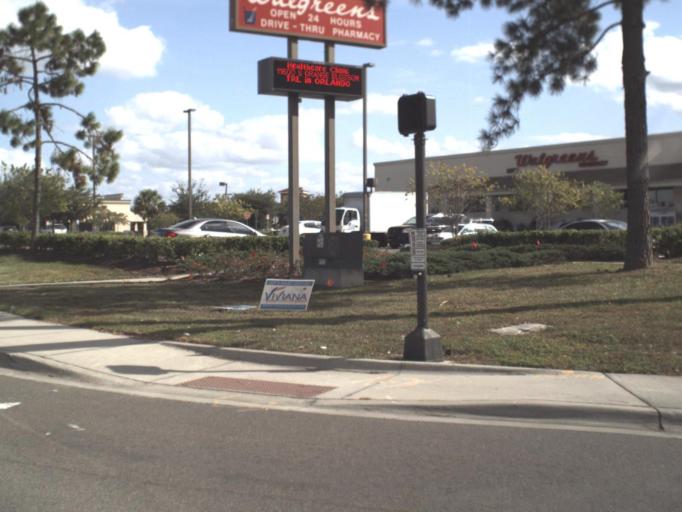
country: US
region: Florida
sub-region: Osceola County
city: Buenaventura Lakes
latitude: 28.3448
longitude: -81.3626
